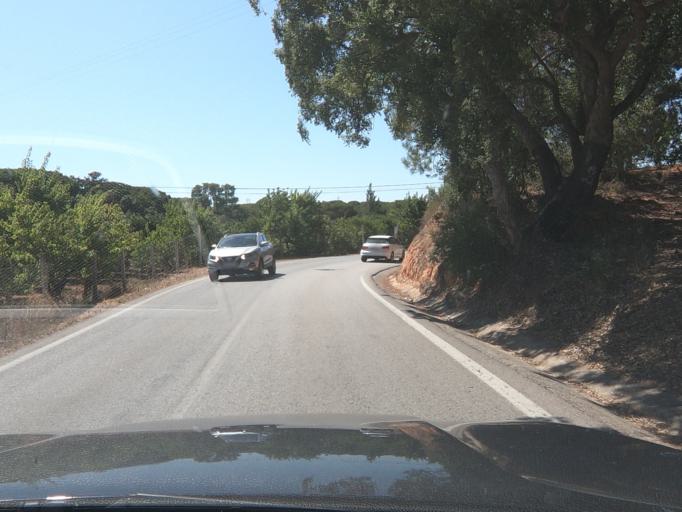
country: PT
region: Faro
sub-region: Loule
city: Vilamoura
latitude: 37.1034
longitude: -8.0971
